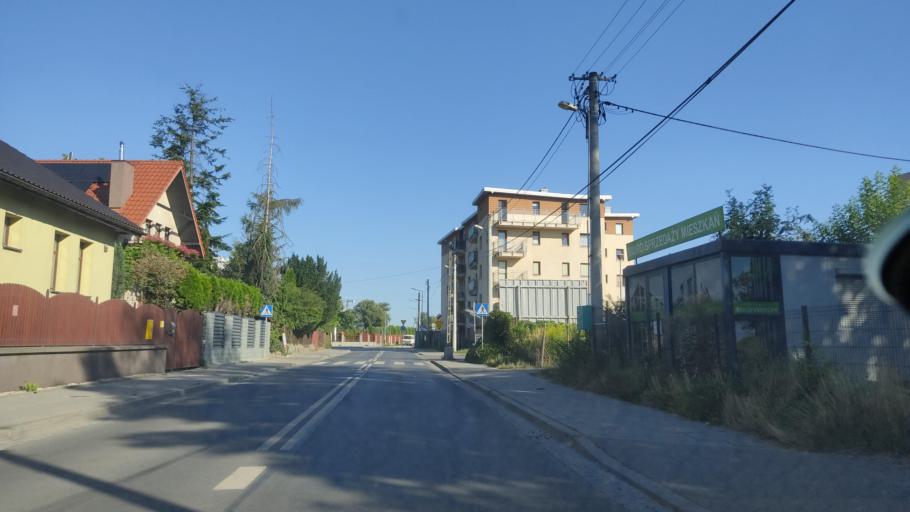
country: PL
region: Lesser Poland Voivodeship
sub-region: Powiat krakowski
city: Zielonki
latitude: 50.0960
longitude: 19.9343
